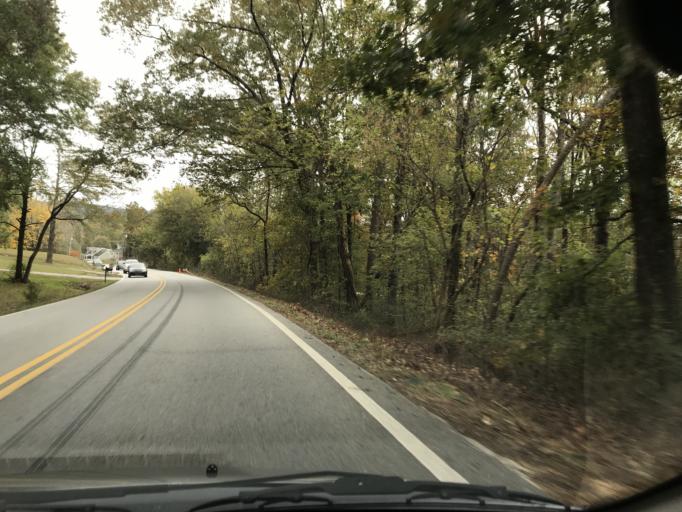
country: US
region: Tennessee
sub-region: Hamilton County
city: Lakesite
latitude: 35.1827
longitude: -85.0572
